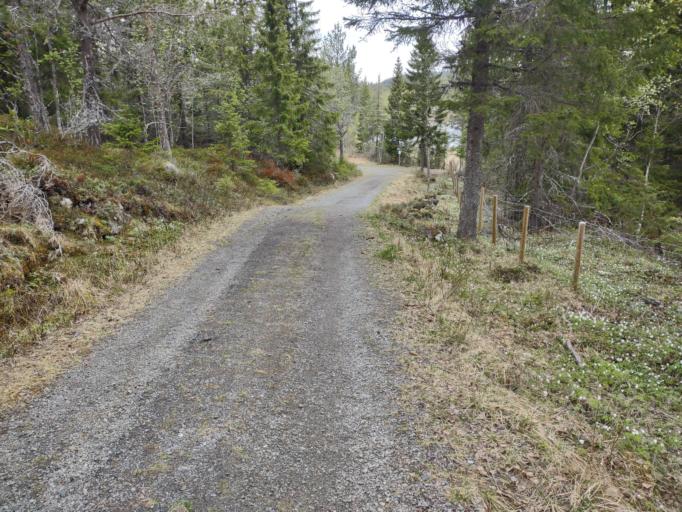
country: NO
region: Oppland
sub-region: Gran
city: Jaren
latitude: 60.4521
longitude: 10.6452
